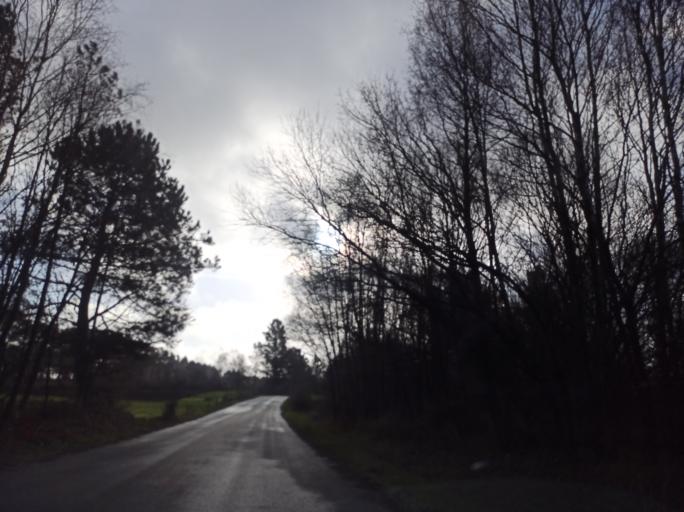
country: ES
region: Galicia
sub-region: Provincia da Coruna
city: Curtis
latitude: 43.0967
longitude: -7.9770
